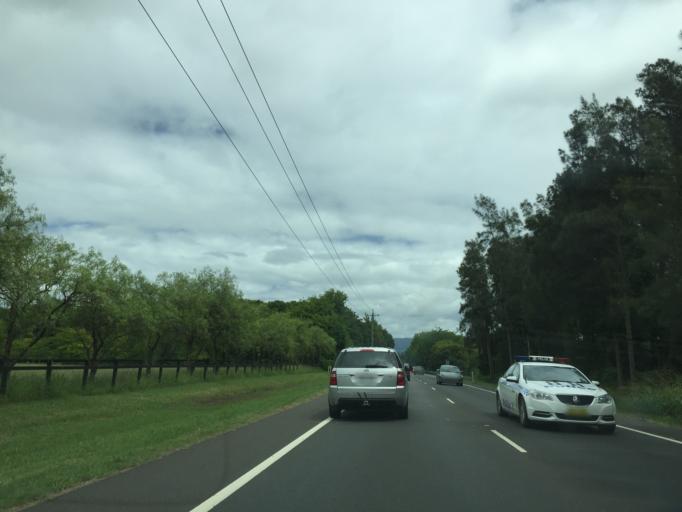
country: AU
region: New South Wales
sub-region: Hawkesbury
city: Richmond
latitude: -33.5917
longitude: 150.7359
